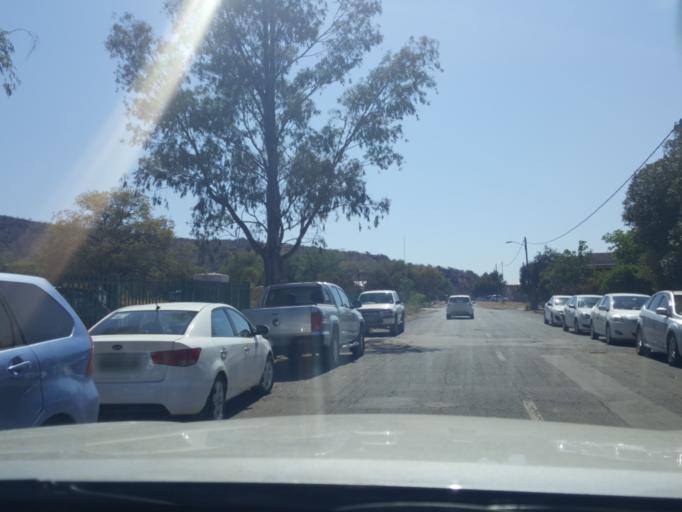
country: ZA
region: North-West
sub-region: Ngaka Modiri Molema District Municipality
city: Zeerust
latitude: -25.5425
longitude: 26.0815
